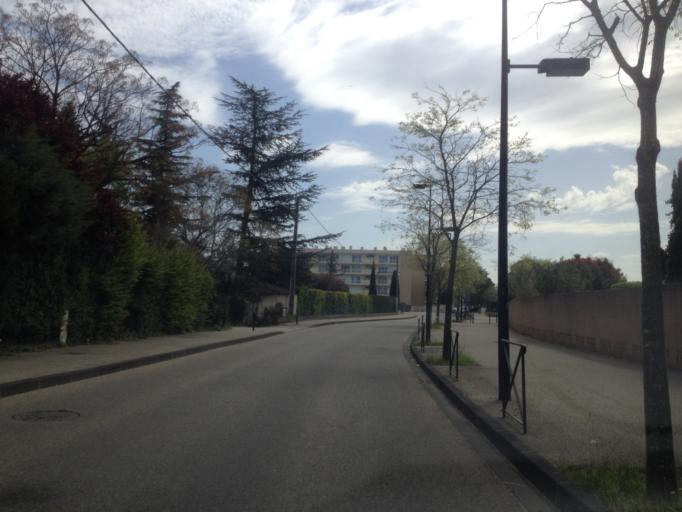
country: FR
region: Provence-Alpes-Cote d'Azur
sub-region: Departement du Vaucluse
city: Orange
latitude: 44.1421
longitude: 4.7958
